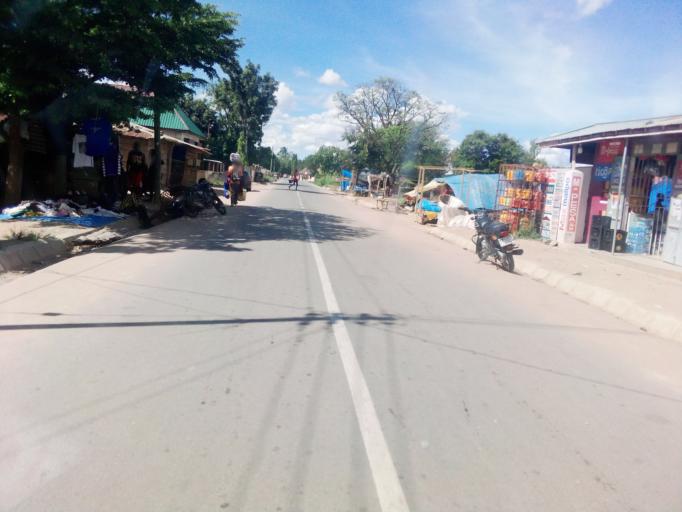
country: TZ
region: Dodoma
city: Dodoma
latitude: -6.1734
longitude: 35.7584
